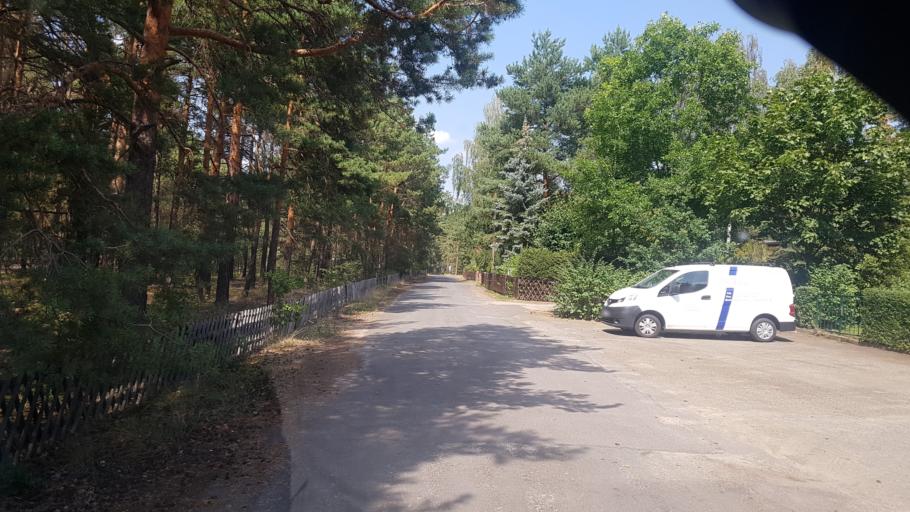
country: DE
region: Brandenburg
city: Spremberg
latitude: 51.6434
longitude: 14.4168
